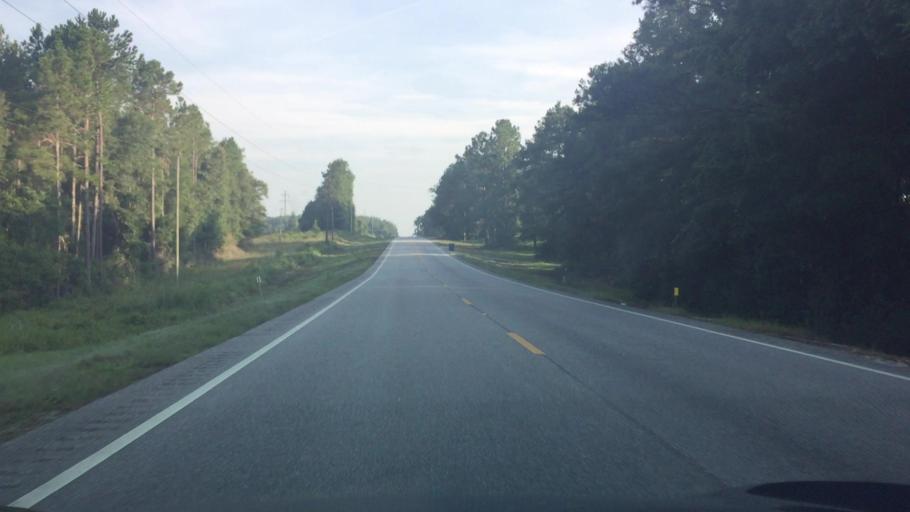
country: US
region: Alabama
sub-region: Covington County
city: Florala
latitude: 31.1266
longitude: -86.4556
